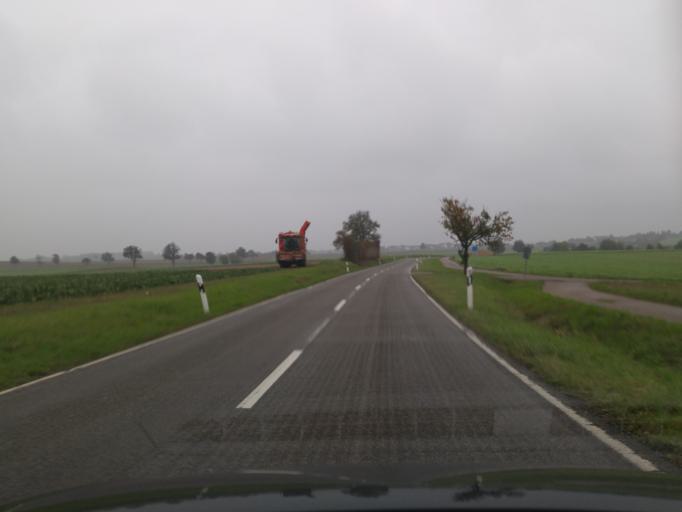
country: DE
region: Baden-Wuerttemberg
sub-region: Regierungsbezirk Stuttgart
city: Bad Wimpfen
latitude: 49.2101
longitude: 9.1484
